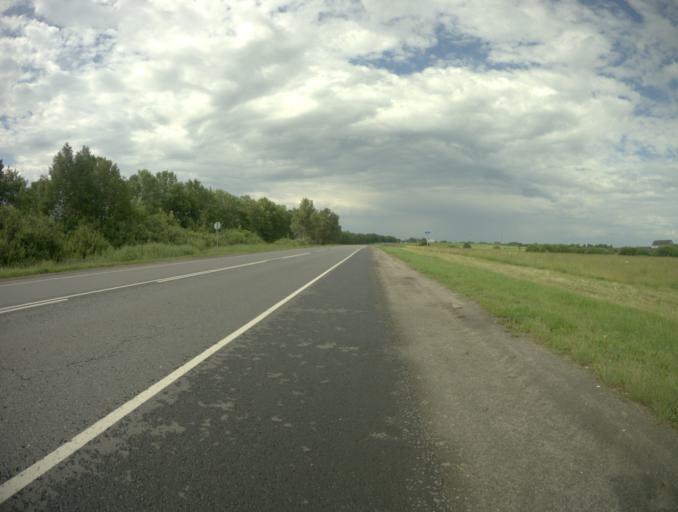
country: RU
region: Vladimir
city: Suzdal'
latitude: 56.3074
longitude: 40.4702
